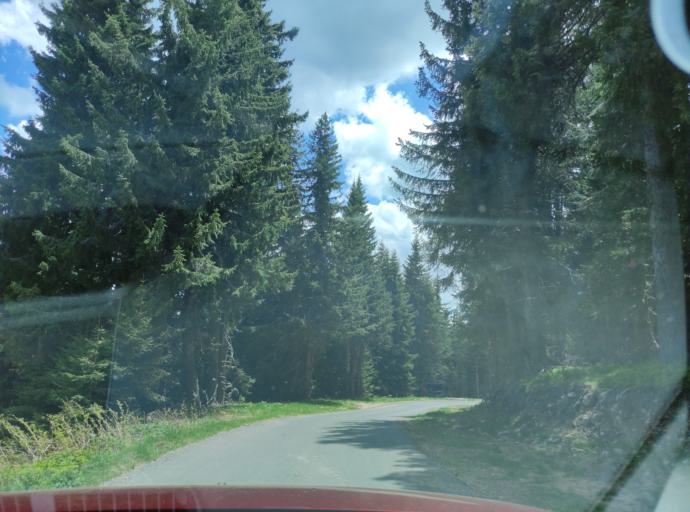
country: BG
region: Smolyan
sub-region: Obshtina Smolyan
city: Smolyan
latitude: 41.6378
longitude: 24.6866
